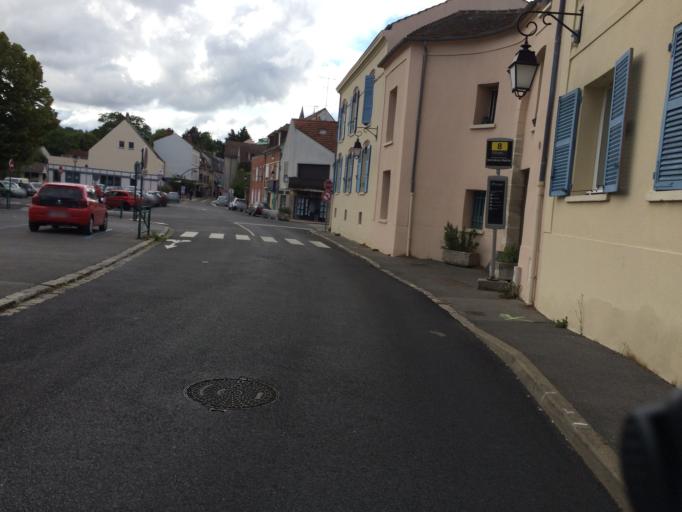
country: FR
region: Ile-de-France
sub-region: Departement de l'Essonne
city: Verrieres-le-Buisson
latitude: 48.7468
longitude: 2.2678
